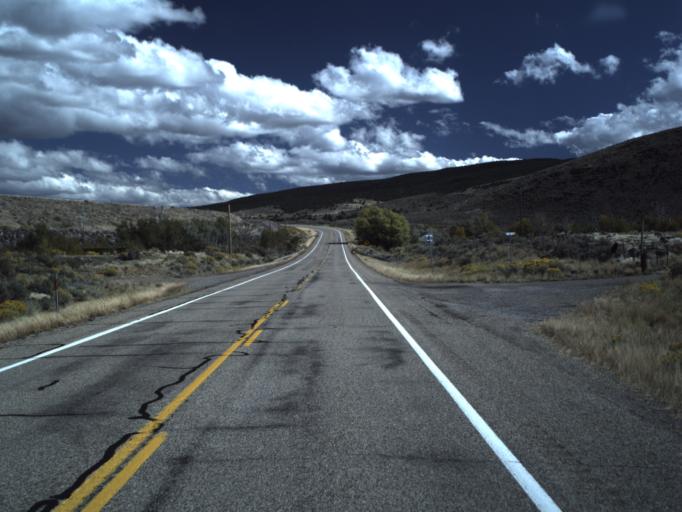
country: US
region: Utah
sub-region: Beaver County
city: Beaver
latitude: 38.2167
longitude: -112.8375
